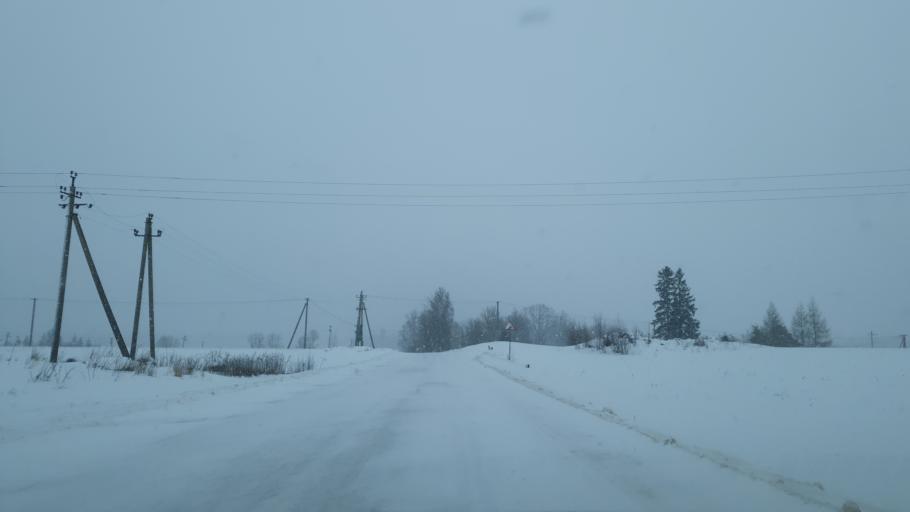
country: EE
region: Jogevamaa
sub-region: Jogeva linn
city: Jogeva
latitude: 58.8218
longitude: 26.3451
